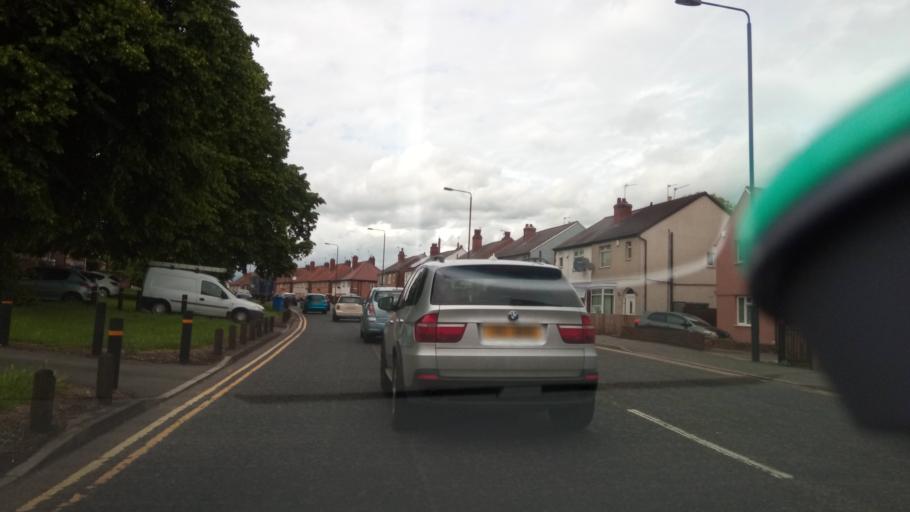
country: GB
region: England
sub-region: Derby
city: Derby
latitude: 52.8943
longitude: -1.4598
